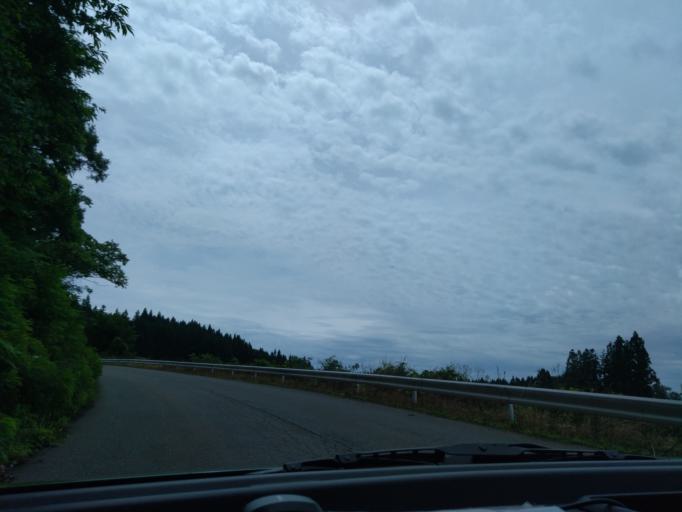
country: JP
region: Akita
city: Kakunodatemachi
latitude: 39.5866
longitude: 140.6187
